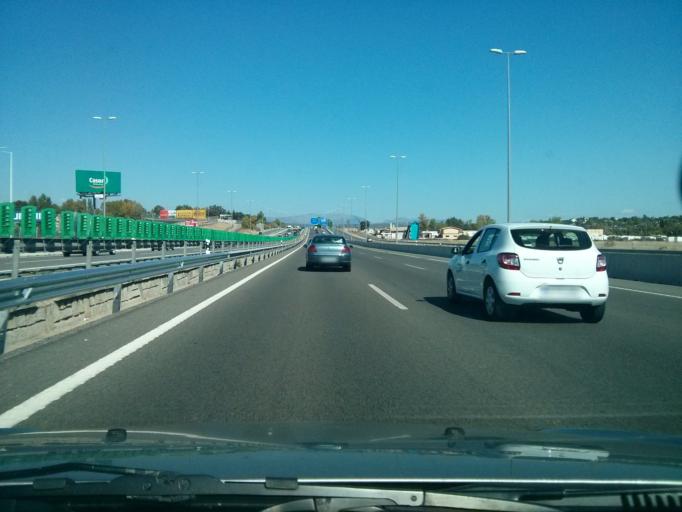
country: ES
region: Madrid
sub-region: Provincia de Madrid
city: San Agustin de Guadalix
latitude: 40.6164
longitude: -3.5829
